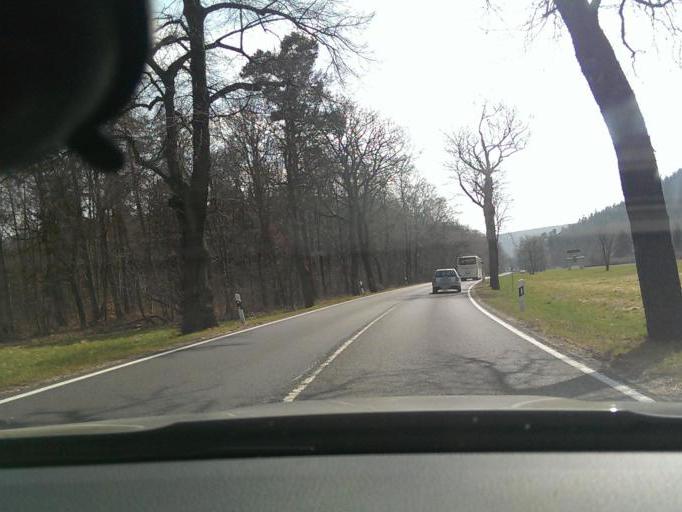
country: DE
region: Thuringia
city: Luisenthal
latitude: 50.7999
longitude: 10.7294
